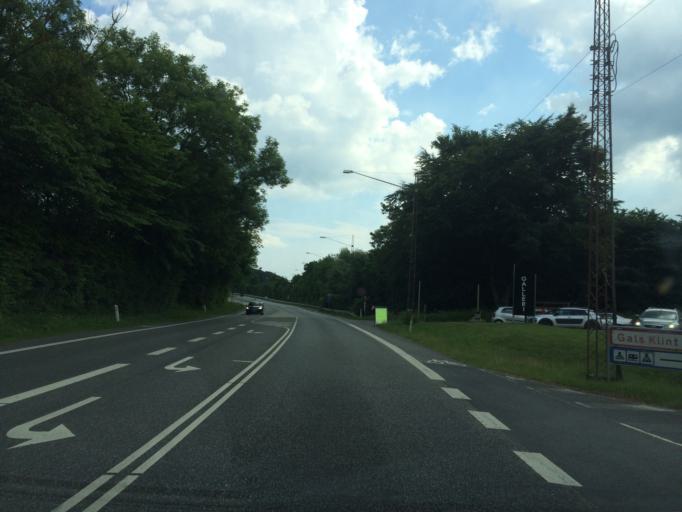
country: DK
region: South Denmark
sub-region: Fredericia Kommune
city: Snoghoj
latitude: 55.5099
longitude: 9.7023
